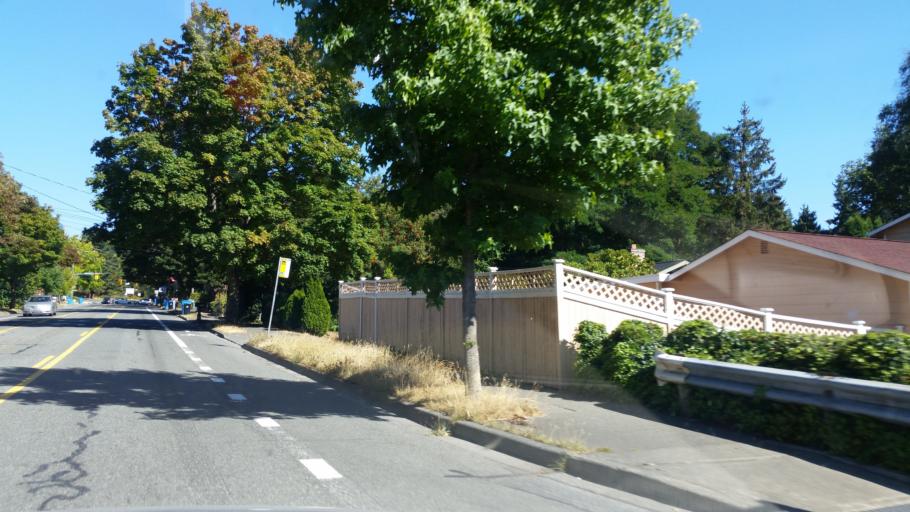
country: US
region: Washington
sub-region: King County
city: Shoreline
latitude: 47.7412
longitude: -122.3158
